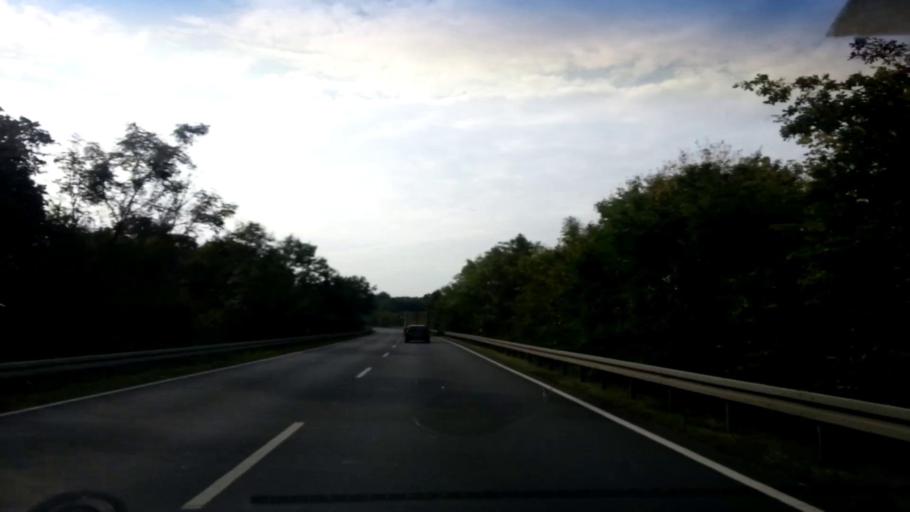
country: DE
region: Bavaria
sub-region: Regierungsbezirk Unterfranken
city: Prichsenstadt
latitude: 49.8349
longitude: 10.3536
